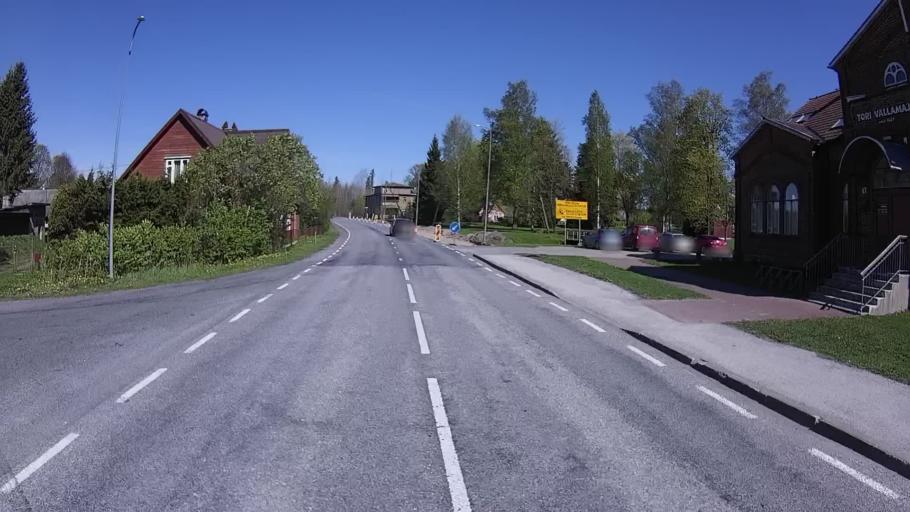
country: EE
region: Paernumaa
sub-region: Tootsi vald
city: Tootsi
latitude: 58.4854
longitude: 24.8141
